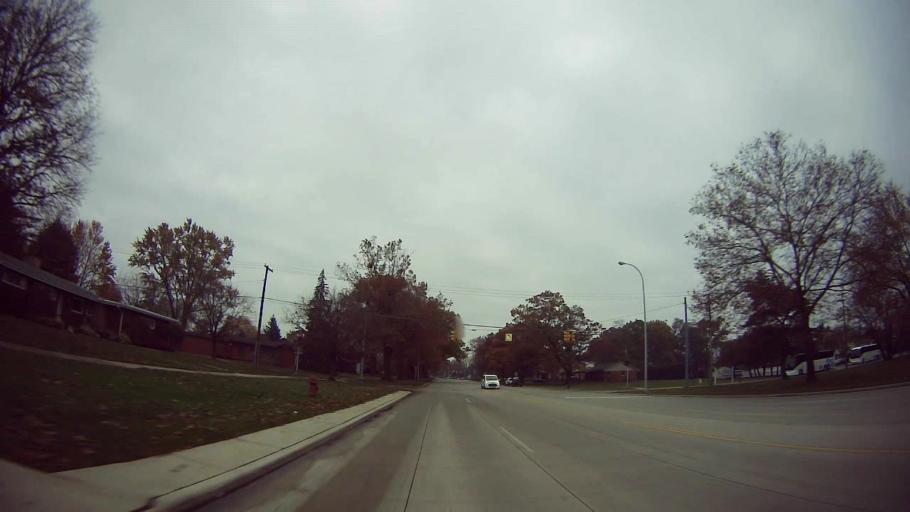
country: US
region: Michigan
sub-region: Wayne County
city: Dearborn Heights
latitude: 42.3300
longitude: -83.2614
